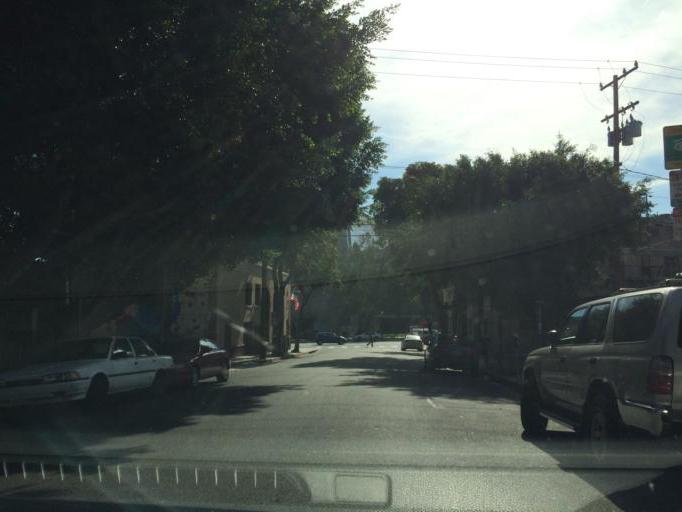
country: US
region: California
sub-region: Los Angeles County
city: Beverly Hills
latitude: 34.0862
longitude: -118.3838
